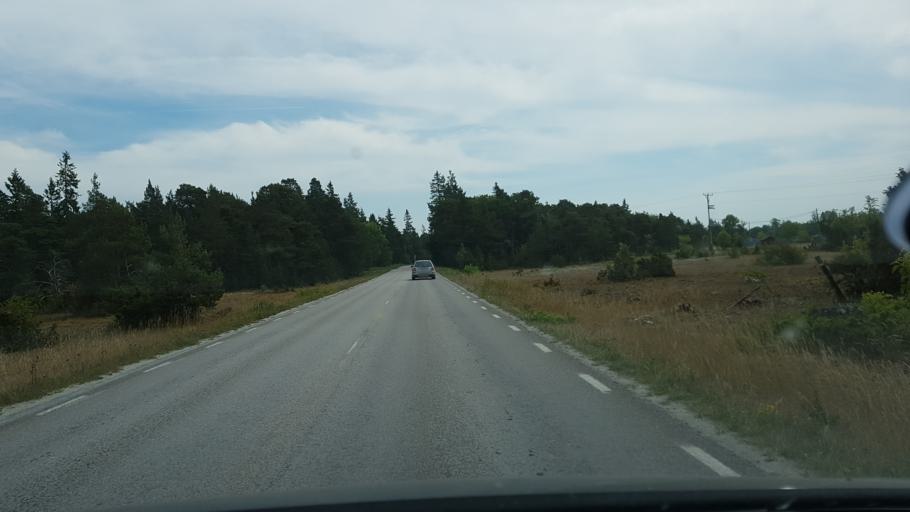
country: SE
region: Gotland
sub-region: Gotland
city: Slite
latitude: 57.7446
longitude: 18.7363
